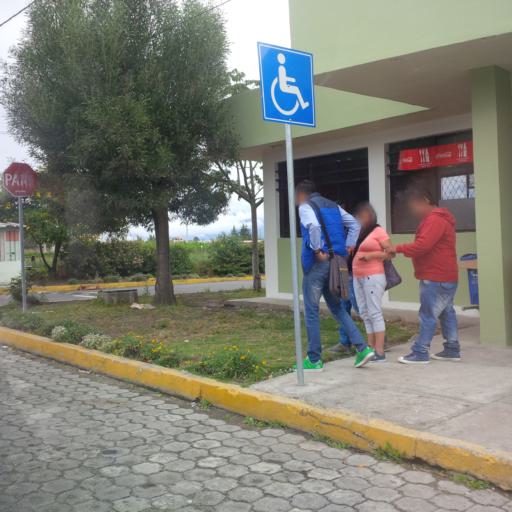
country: EC
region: Chimborazo
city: Riobamba
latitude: -1.6519
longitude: -78.6826
